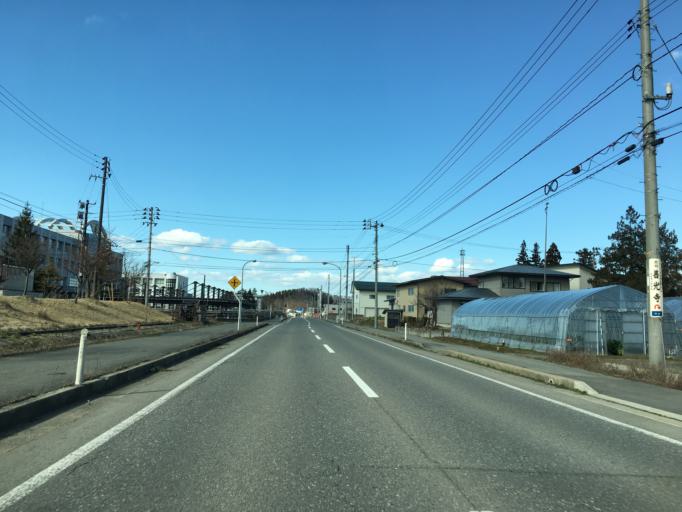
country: JP
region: Yamagata
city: Yonezawa
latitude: 37.9152
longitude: 140.1461
